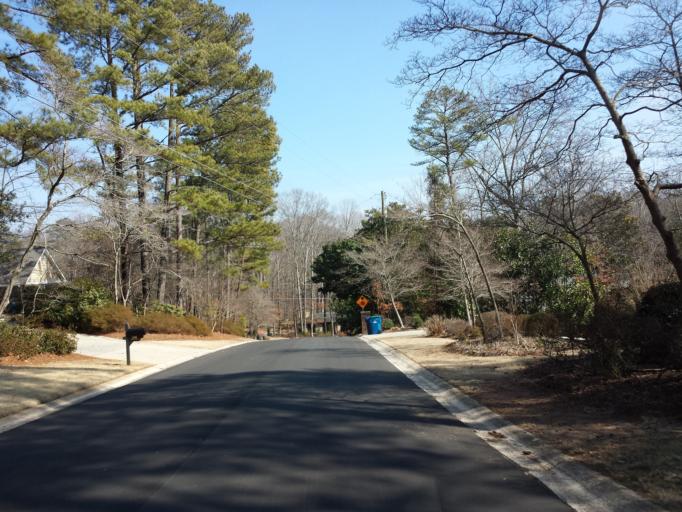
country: US
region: Georgia
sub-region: Cobb County
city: Vinings
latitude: 33.9178
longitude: -84.4591
